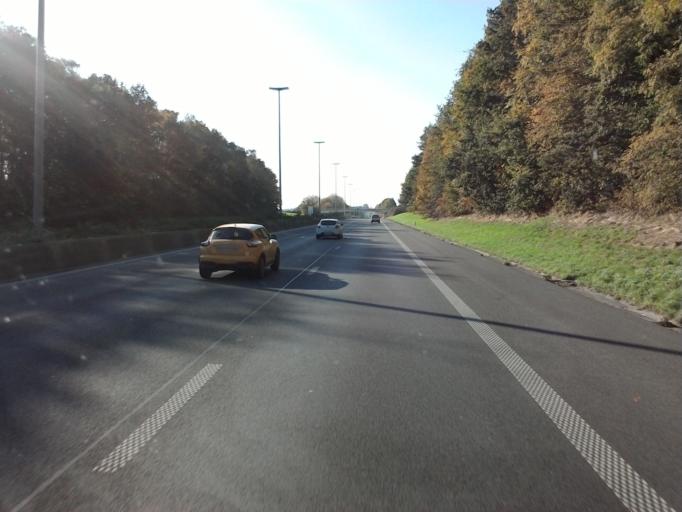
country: BE
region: Wallonia
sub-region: Province de Namur
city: Gembloux
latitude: 50.4944
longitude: 4.6880
